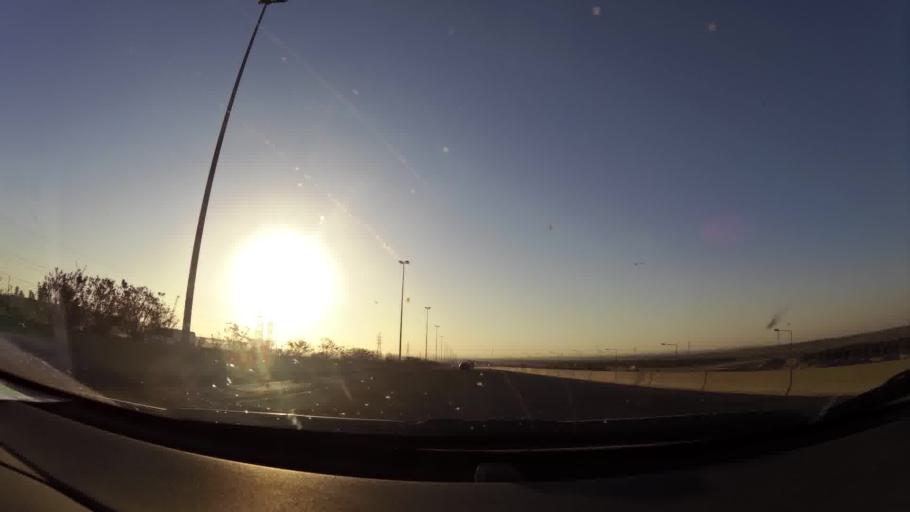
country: KW
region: Al Ahmadi
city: Al Fahahil
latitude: 28.9952
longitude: 48.1438
